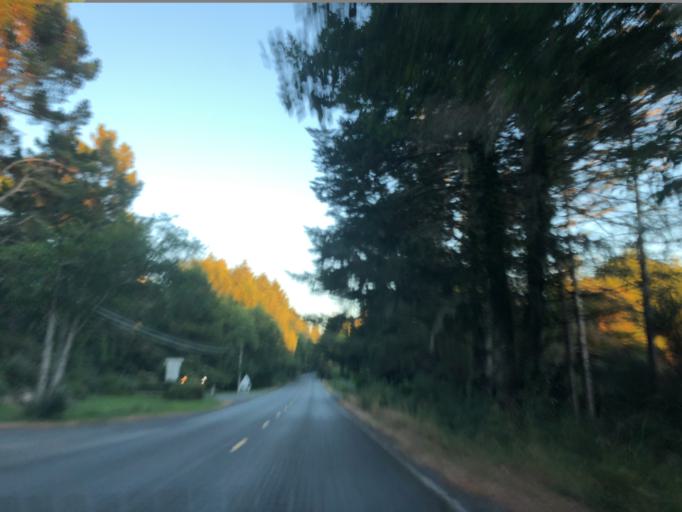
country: US
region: California
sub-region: Humboldt County
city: Westhaven-Moonstone
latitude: 41.0942
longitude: -124.1557
